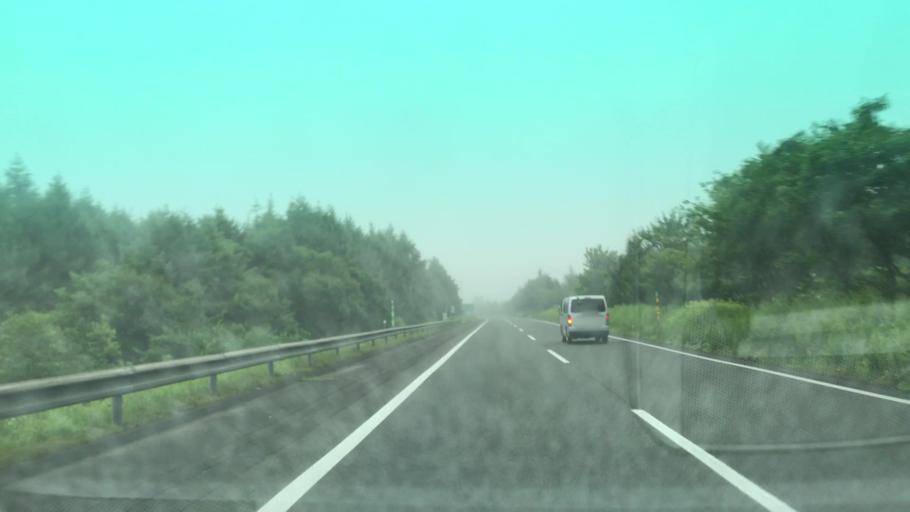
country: JP
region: Hokkaido
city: Chitose
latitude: 42.7901
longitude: 141.6267
